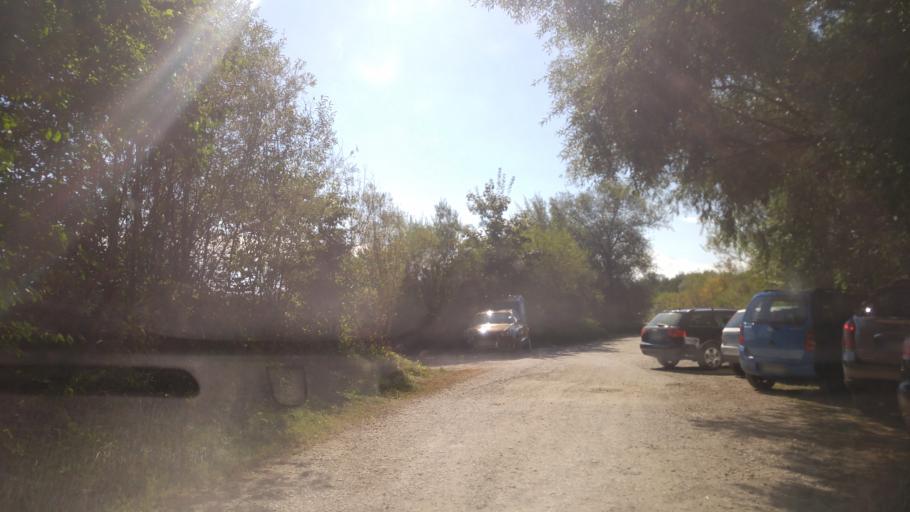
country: DE
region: Bavaria
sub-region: Swabia
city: Guenzburg
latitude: 48.4786
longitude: 10.2865
